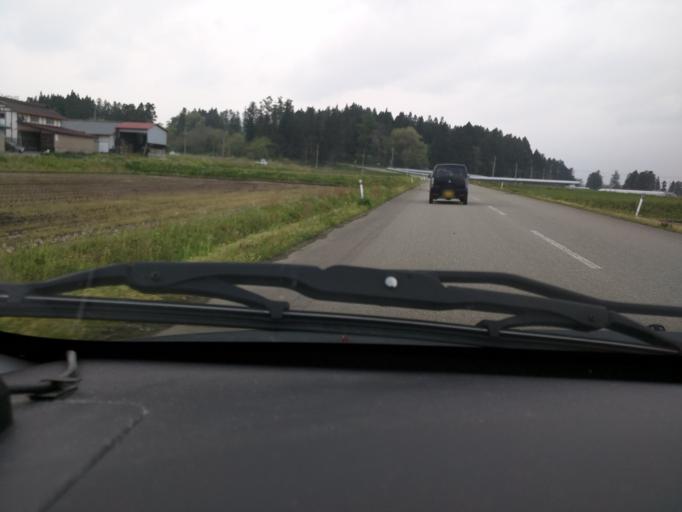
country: JP
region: Fukushima
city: Kitakata
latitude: 37.4971
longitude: 139.8208
